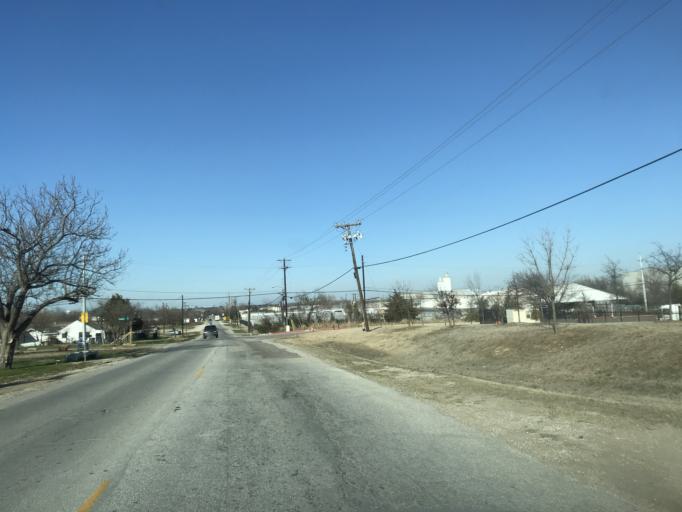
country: US
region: Texas
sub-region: Dallas County
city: Cockrell Hill
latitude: 32.7684
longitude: -96.9026
